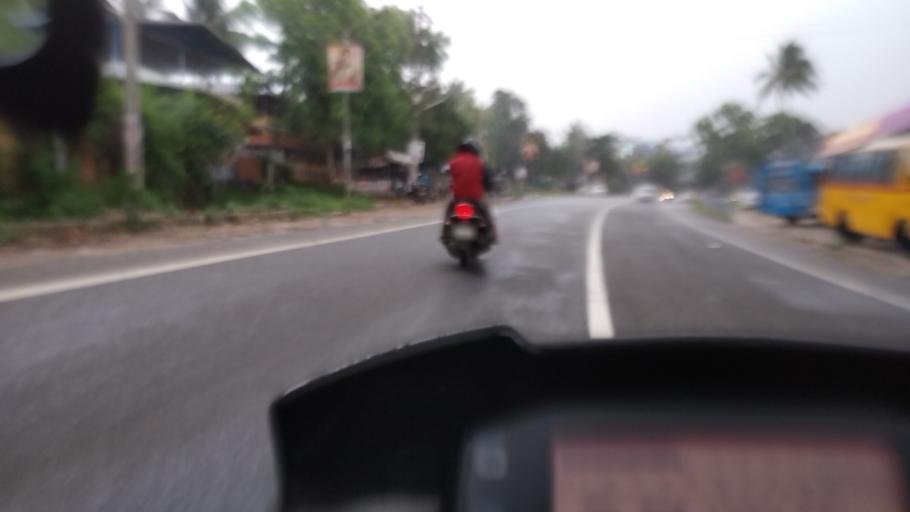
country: IN
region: Kerala
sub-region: Thiruvananthapuram
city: Attingal
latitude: 8.7120
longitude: 76.8118
